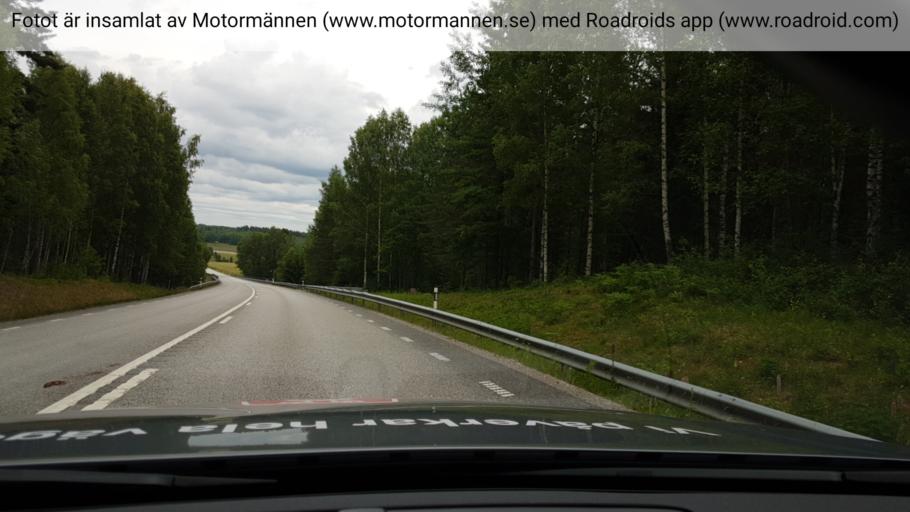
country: SE
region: OErebro
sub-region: Lindesbergs Kommun
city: Lindesberg
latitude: 59.6222
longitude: 15.2074
